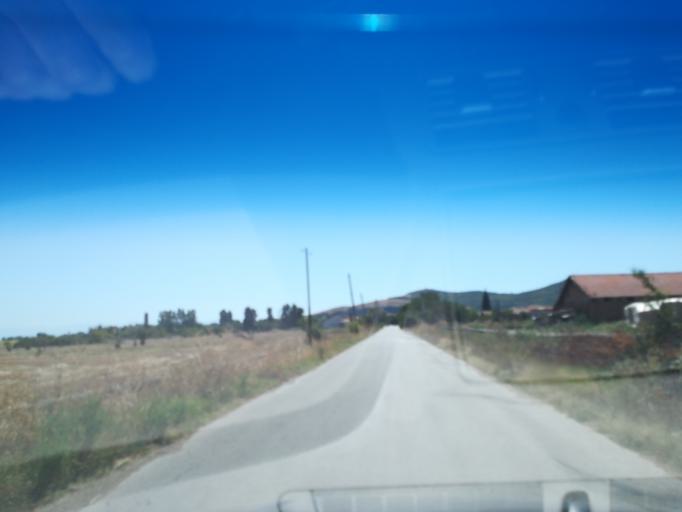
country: BG
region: Pazardzhik
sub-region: Obshtina Pazardzhik
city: Pazardzhik
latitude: 42.3443
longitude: 24.4006
